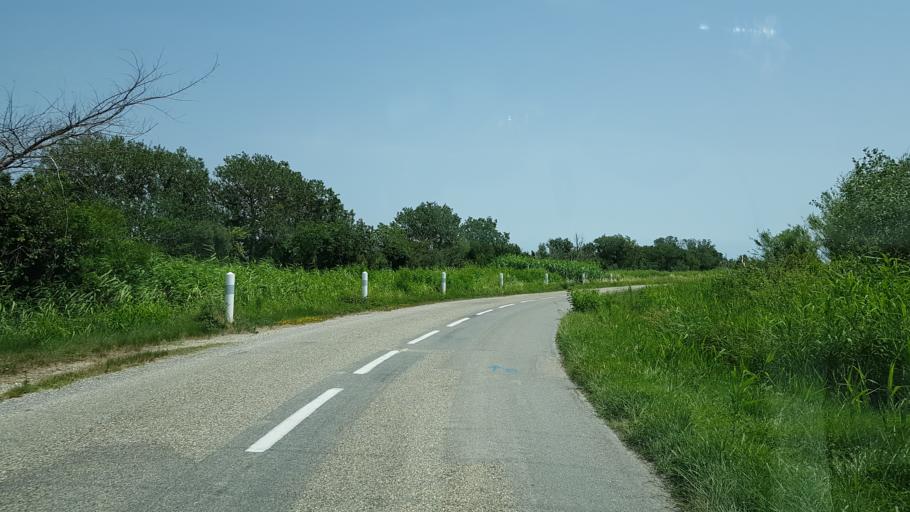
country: FR
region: Provence-Alpes-Cote d'Azur
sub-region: Departement des Bouches-du-Rhone
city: Port-Saint-Louis-du-Rhone
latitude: 43.4444
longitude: 4.6745
